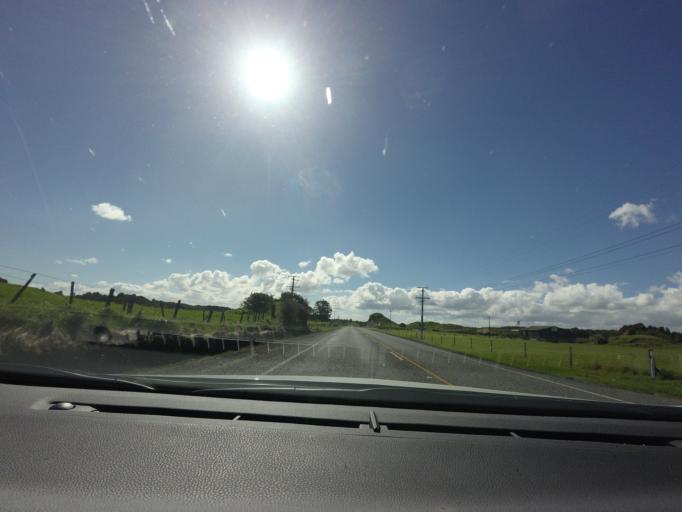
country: NZ
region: Bay of Plenty
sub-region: Rotorua District
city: Rotorua
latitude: -38.0488
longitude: 176.0745
